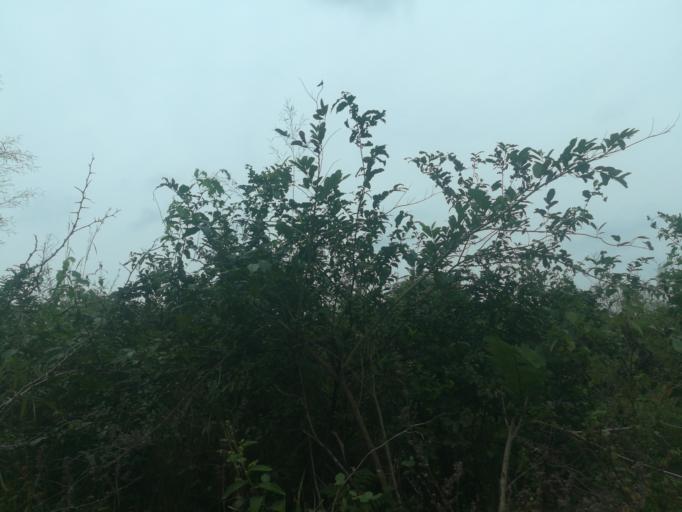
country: NG
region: Ogun
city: Itori
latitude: 7.1028
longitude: 3.1498
